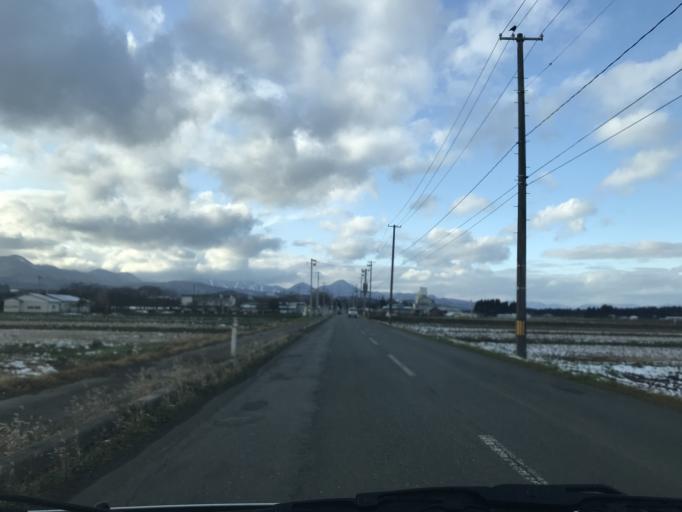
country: JP
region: Iwate
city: Kitakami
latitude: 39.2025
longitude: 141.0549
